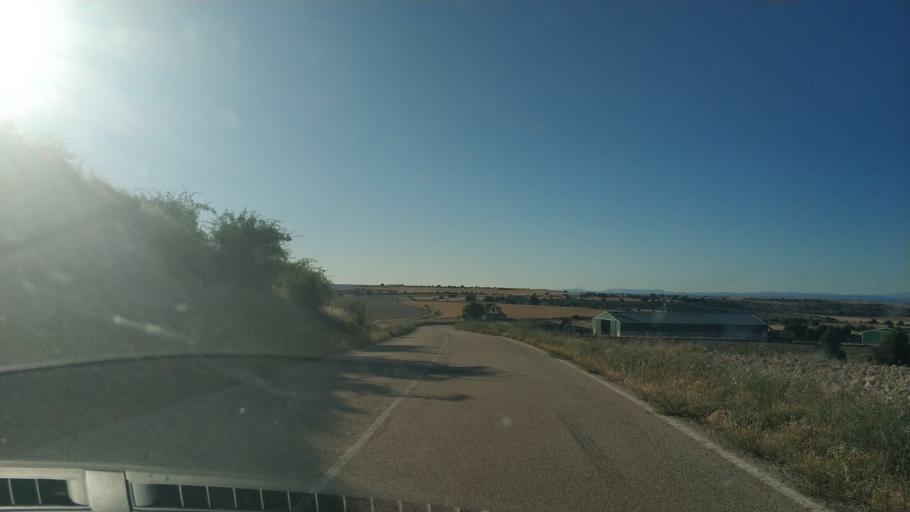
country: ES
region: Castille and Leon
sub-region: Provincia de Soria
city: Liceras
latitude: 41.4658
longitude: -3.2157
